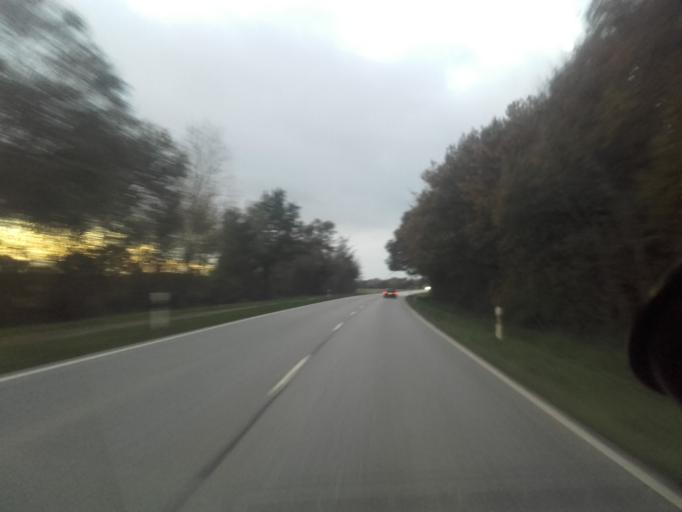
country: DE
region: Schleswig-Holstein
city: Silberstedt
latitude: 54.5161
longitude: 9.4086
